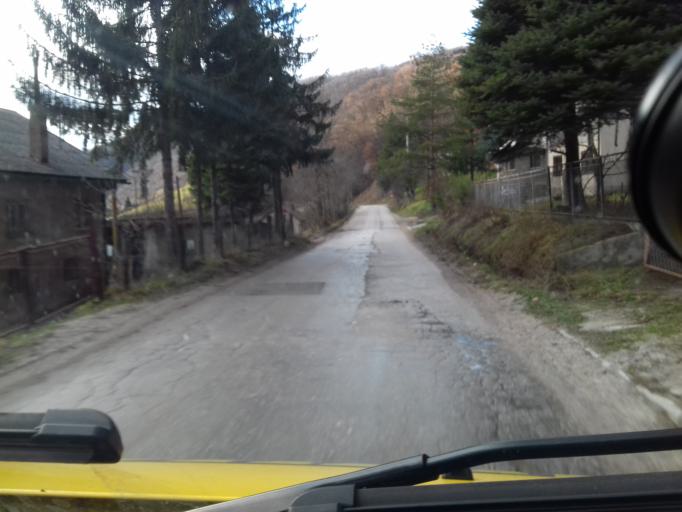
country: BA
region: Federation of Bosnia and Herzegovina
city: Zenica
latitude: 44.2195
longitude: 17.9606
